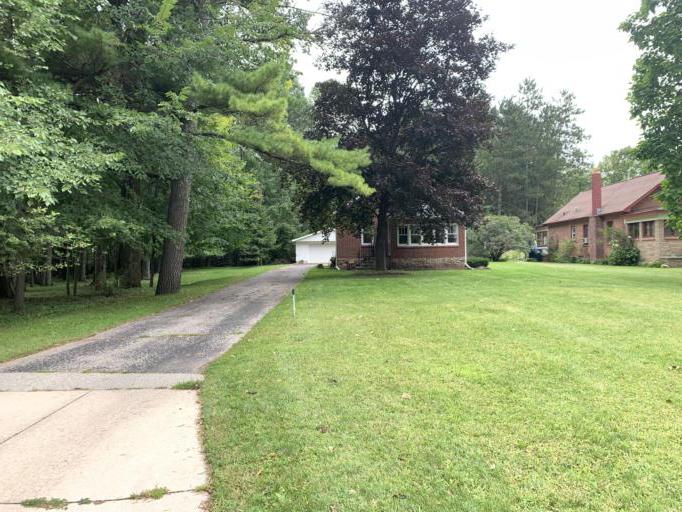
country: US
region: Wisconsin
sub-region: Oconto County
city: Oconto Falls
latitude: 45.0651
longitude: -88.0248
